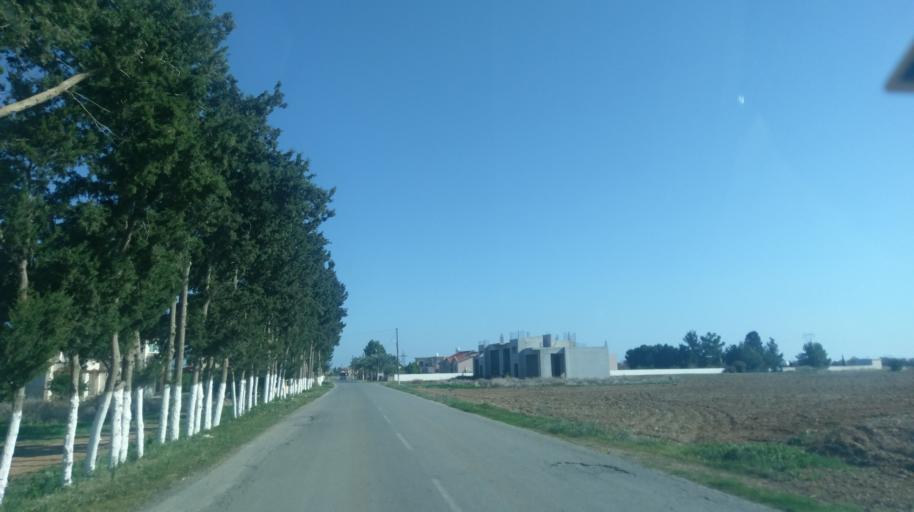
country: CY
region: Ammochostos
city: Trikomo
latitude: 35.2325
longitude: 33.8785
